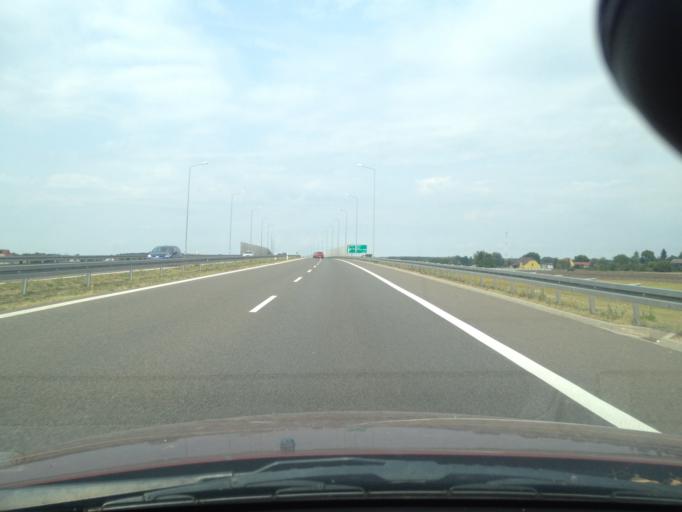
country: PL
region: West Pomeranian Voivodeship
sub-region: Powiat pyrzycki
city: Lipiany
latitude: 52.9474
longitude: 14.9626
